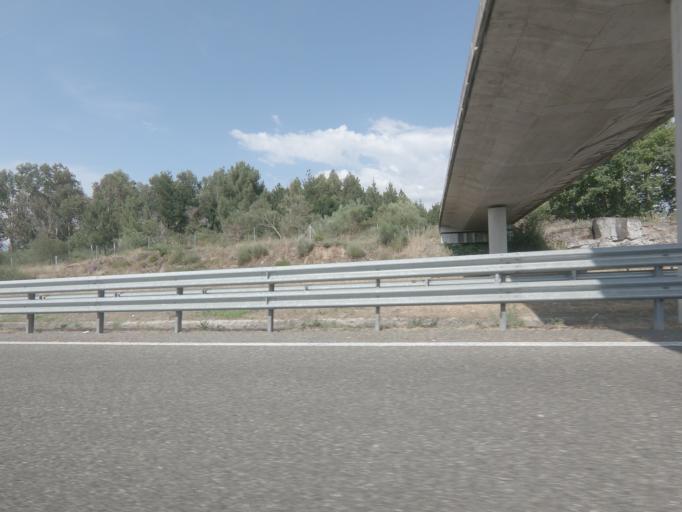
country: ES
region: Galicia
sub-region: Provincia de Ourense
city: Taboadela
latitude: 42.2670
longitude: -7.8702
